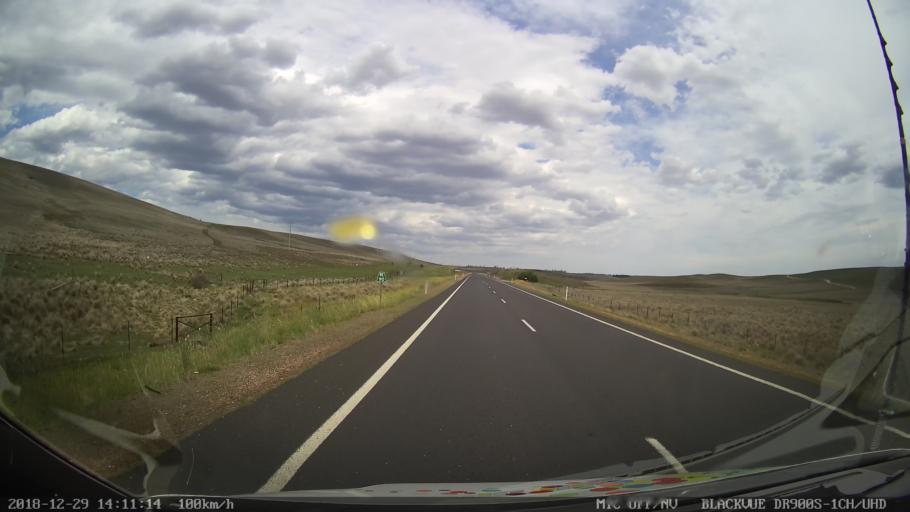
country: AU
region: New South Wales
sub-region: Cooma-Monaro
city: Cooma
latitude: -36.4030
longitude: 149.2190
